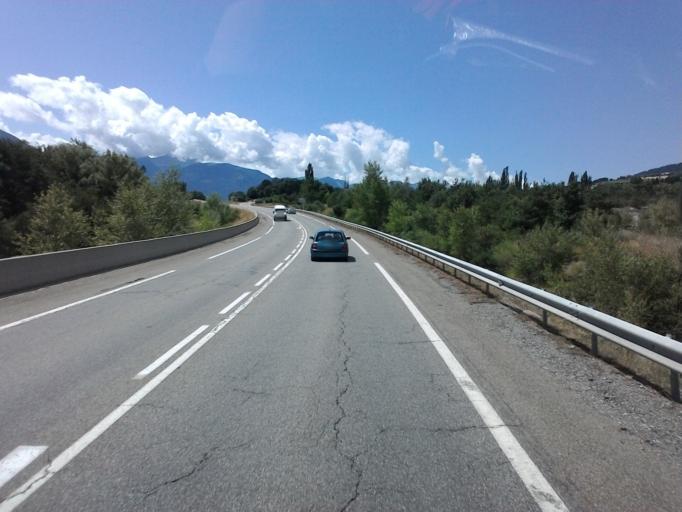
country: FR
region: Provence-Alpes-Cote d'Azur
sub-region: Departement des Hautes-Alpes
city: Embrun
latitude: 44.6196
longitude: 6.5336
